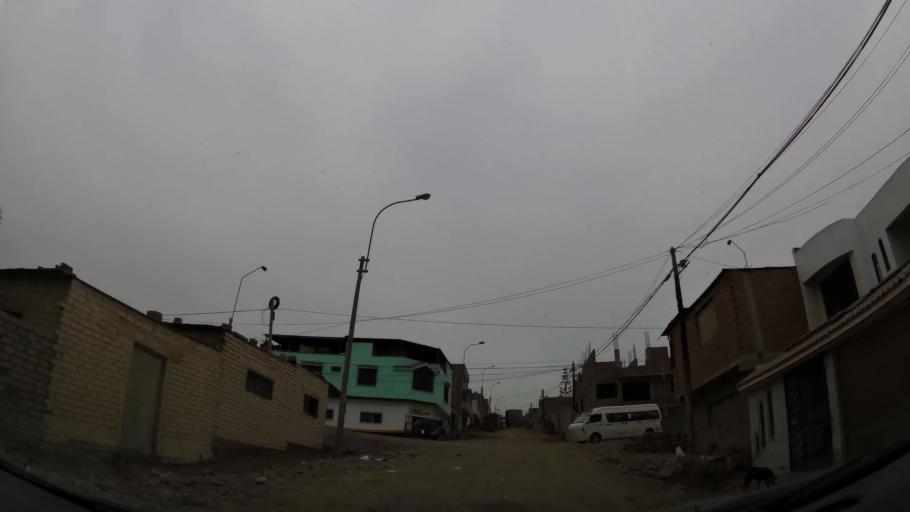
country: PE
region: Lima
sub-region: Lima
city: Surco
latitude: -12.2003
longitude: -76.9842
